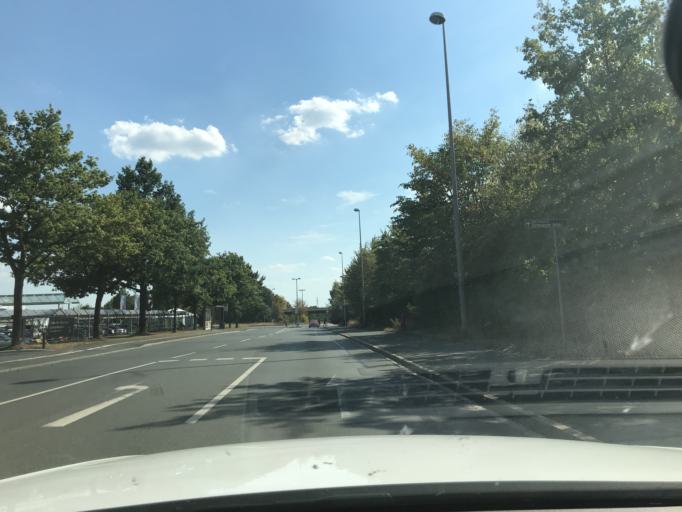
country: DE
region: Bavaria
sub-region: Regierungsbezirk Mittelfranken
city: Erlangen
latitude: 49.5765
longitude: 10.9675
